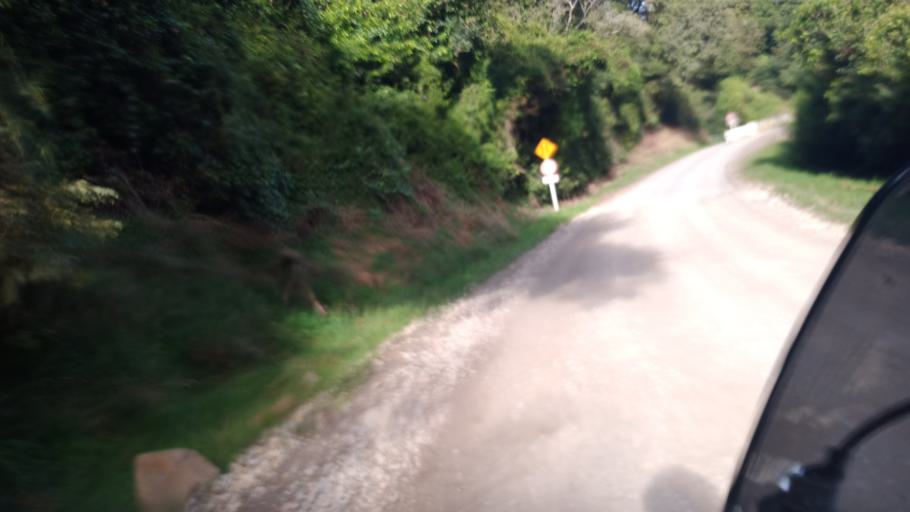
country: NZ
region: Gisborne
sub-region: Gisborne District
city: Gisborne
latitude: -38.5347
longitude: 177.5287
